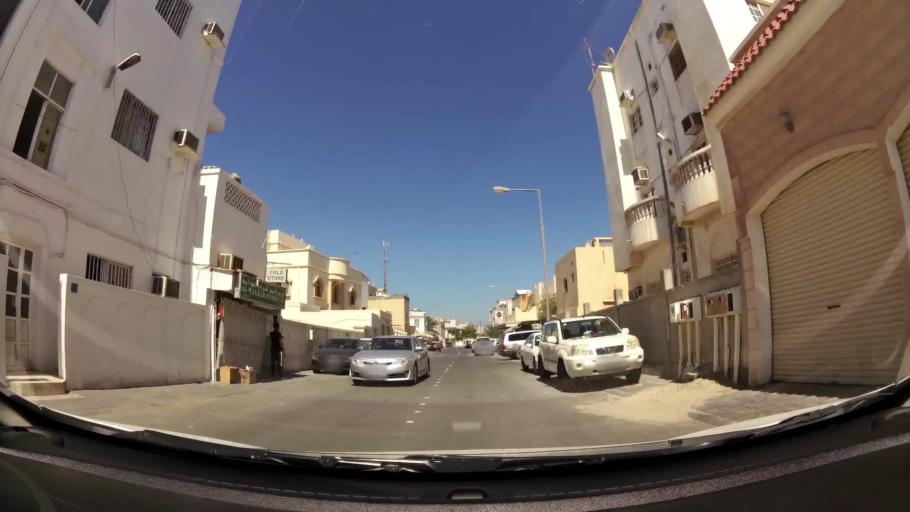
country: BH
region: Muharraq
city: Al Muharraq
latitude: 26.2674
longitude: 50.6060
